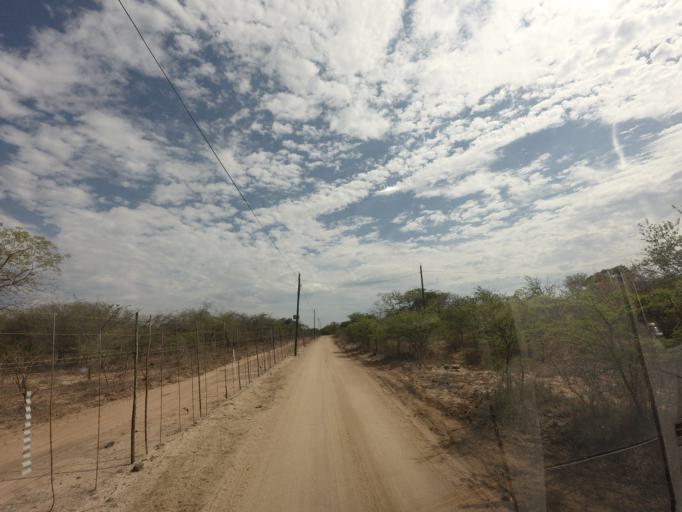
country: ZA
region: Limpopo
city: Thulamahashi
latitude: -24.5177
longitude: 31.1133
